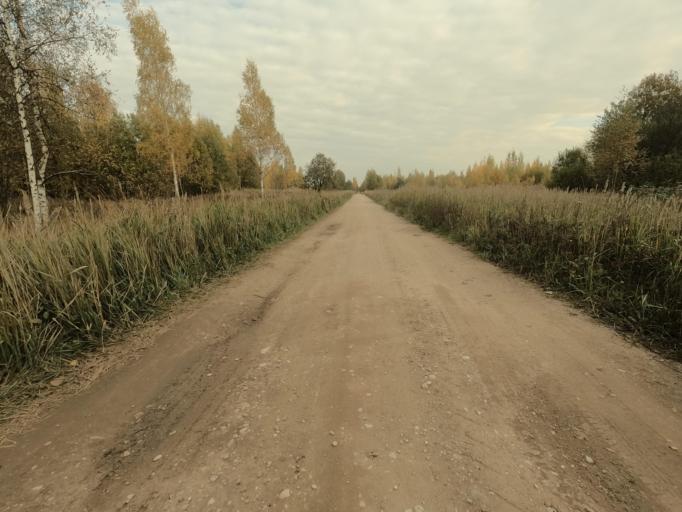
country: RU
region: Novgorod
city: Pankovka
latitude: 58.8985
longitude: 30.9926
